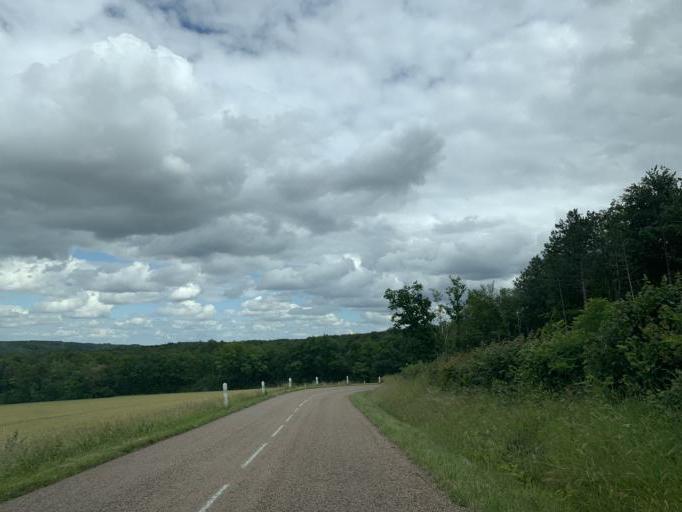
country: FR
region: Bourgogne
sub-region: Departement de l'Yonne
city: Saint-Bris-le-Vineux
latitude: 47.7206
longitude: 3.6898
